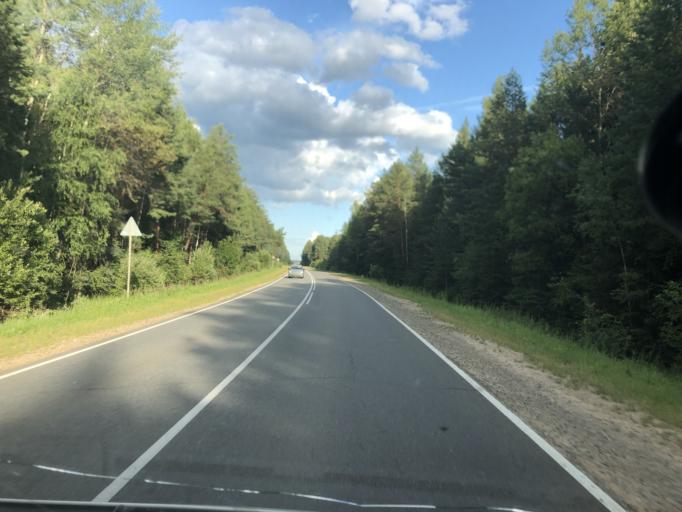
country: RU
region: Kaluga
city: Yukhnov
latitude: 54.7135
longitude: 35.2406
